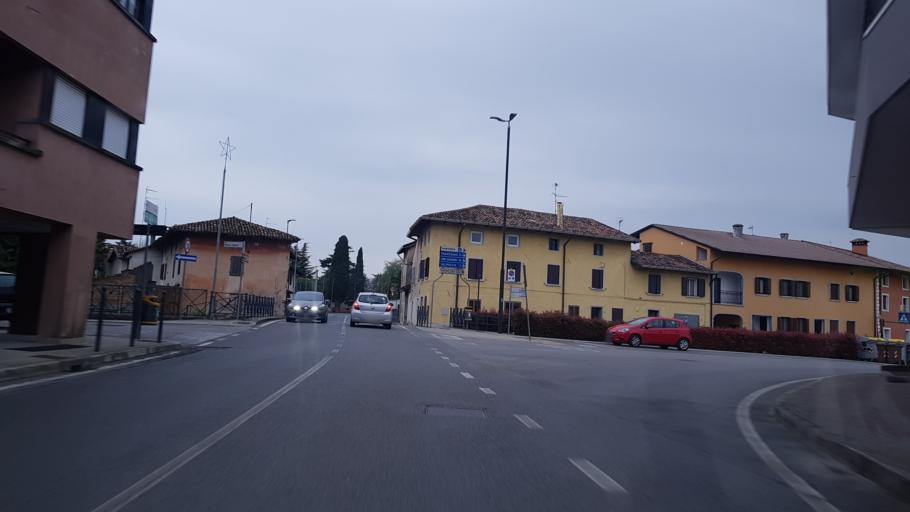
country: IT
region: Friuli Venezia Giulia
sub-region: Provincia di Udine
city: Visco
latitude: 45.8921
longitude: 13.3468
